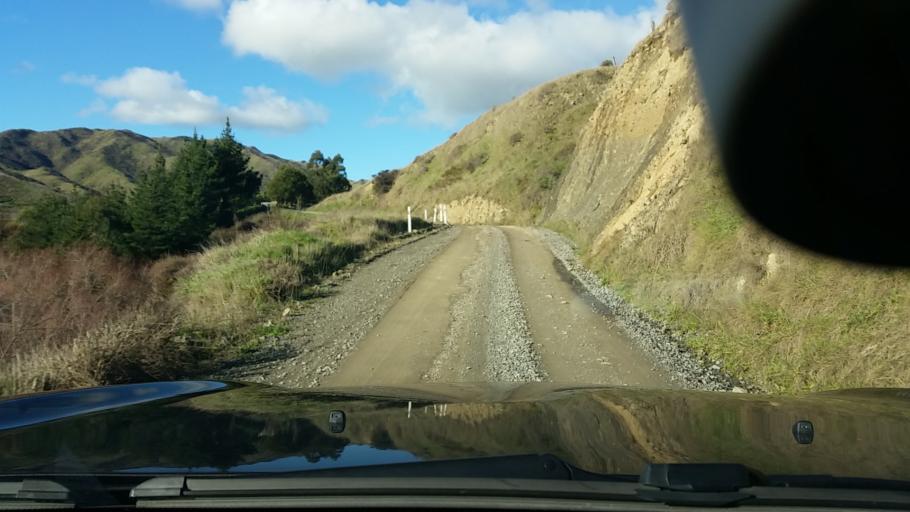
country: NZ
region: Marlborough
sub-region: Marlborough District
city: Blenheim
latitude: -41.6039
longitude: 173.9605
